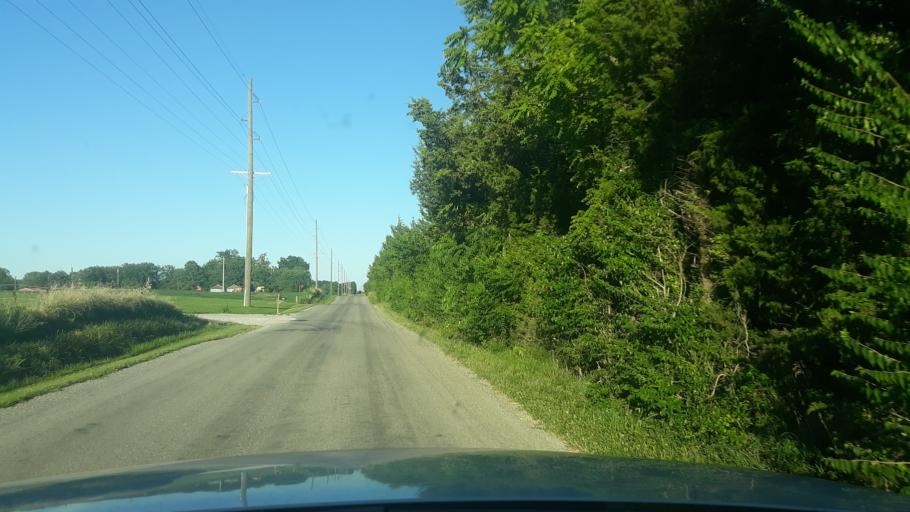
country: US
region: Illinois
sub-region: Saline County
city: Eldorado
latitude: 37.8630
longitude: -88.5518
